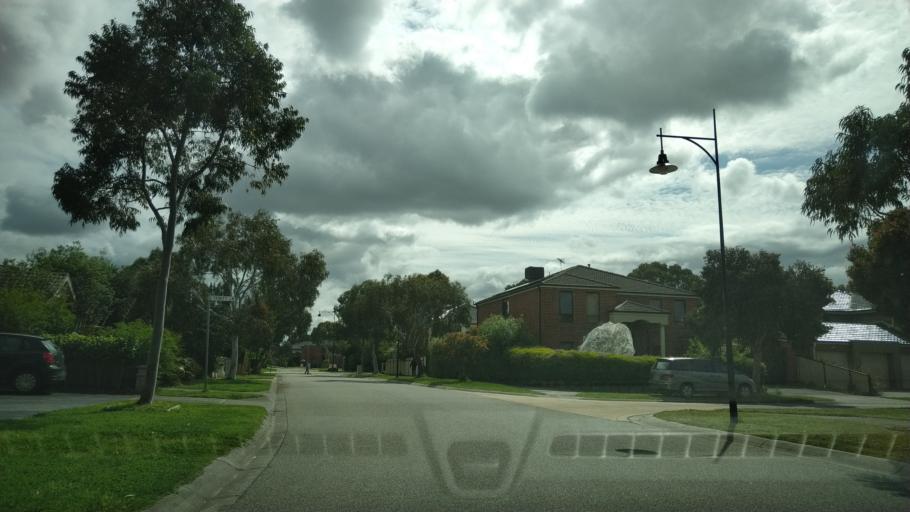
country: AU
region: Victoria
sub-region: Kingston
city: Waterways
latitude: -38.0014
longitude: 145.1466
